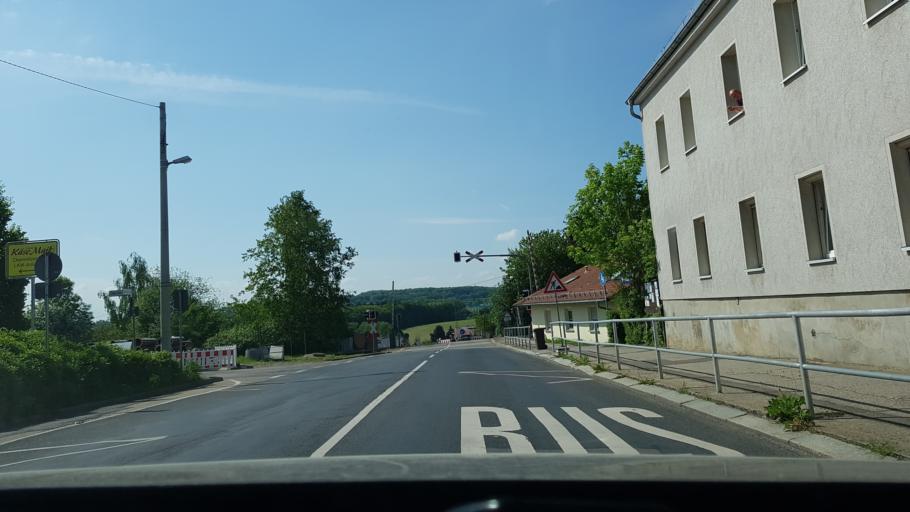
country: DE
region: Saxony
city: Wittgensdorf
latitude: 50.8751
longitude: 12.8707
